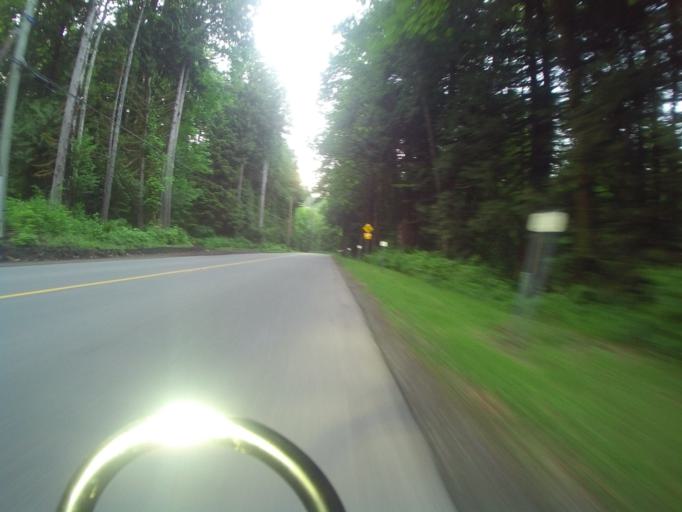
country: CA
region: British Columbia
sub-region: Fraser Valley Regional District
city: Chilliwack
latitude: 49.2861
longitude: -121.9466
